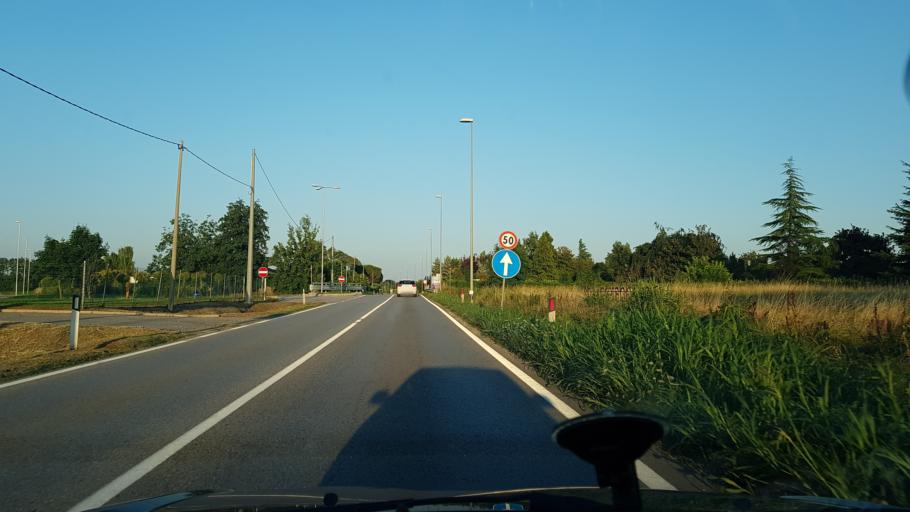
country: IT
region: Friuli Venezia Giulia
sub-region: Provincia di Udine
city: Martignacco
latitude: 46.0881
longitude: 13.1522
